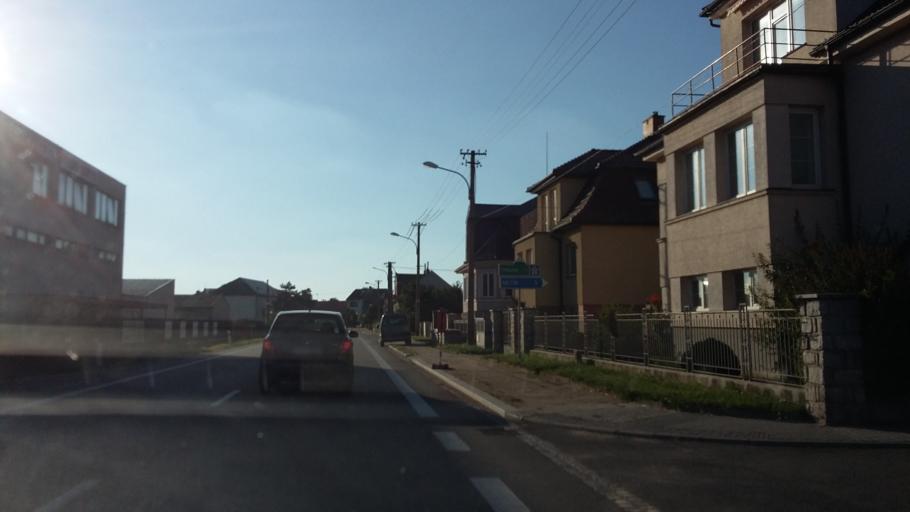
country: CZ
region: Vysocina
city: Merin
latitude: 49.3899
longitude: 15.8938
